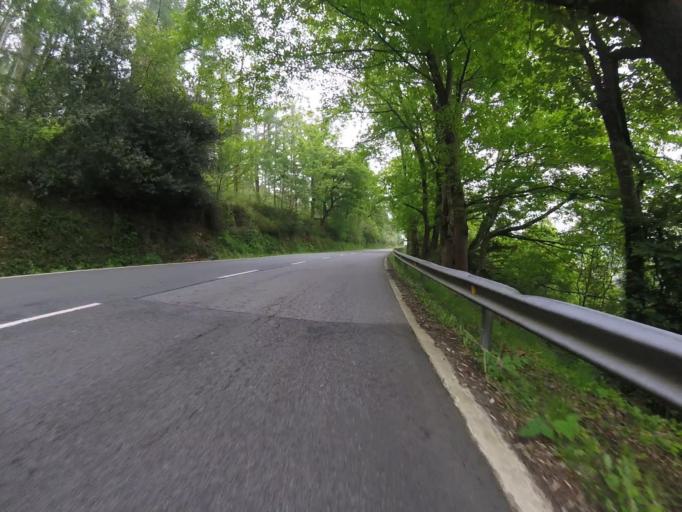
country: ES
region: Navarre
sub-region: Provincia de Navarra
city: Zugarramurdi
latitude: 43.2619
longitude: -1.4887
